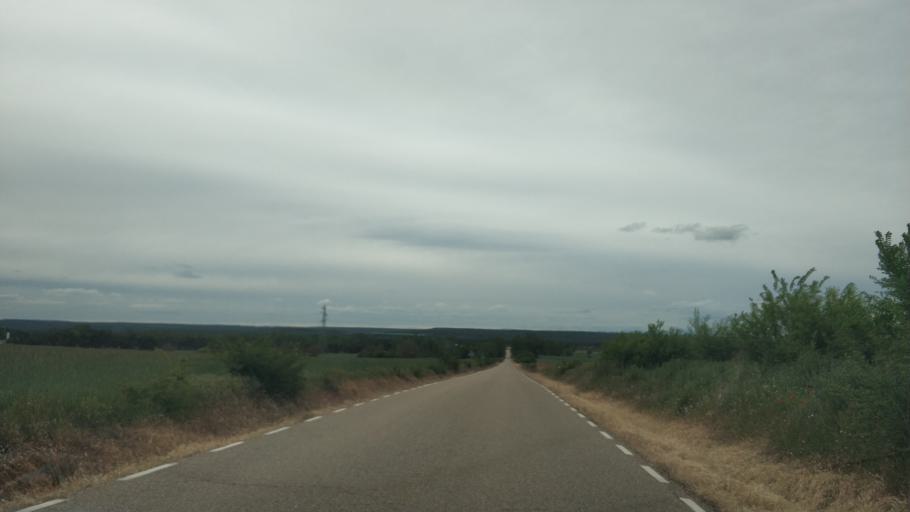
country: ES
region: Castille and Leon
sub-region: Provincia de Soria
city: Berlanga de Duero
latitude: 41.4820
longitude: -2.8646
